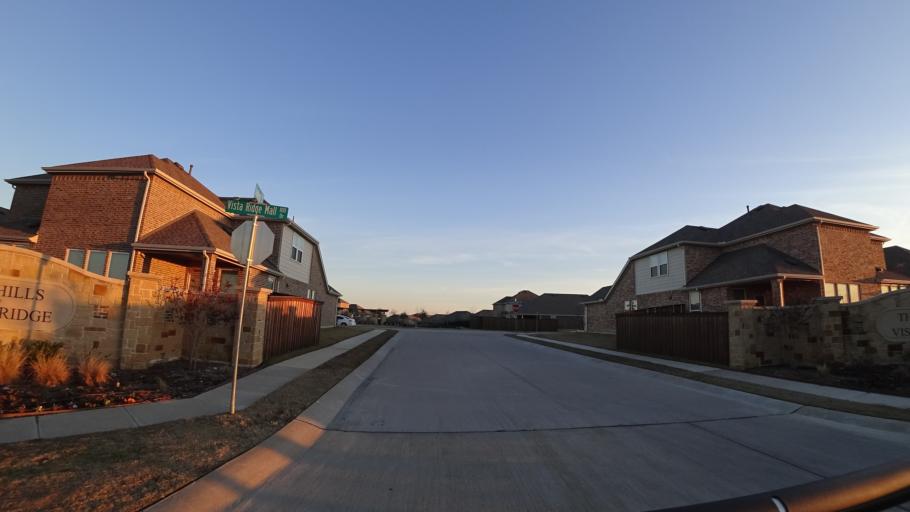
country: US
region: Texas
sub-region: Dallas County
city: Coppell
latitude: 32.9967
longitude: -96.9893
